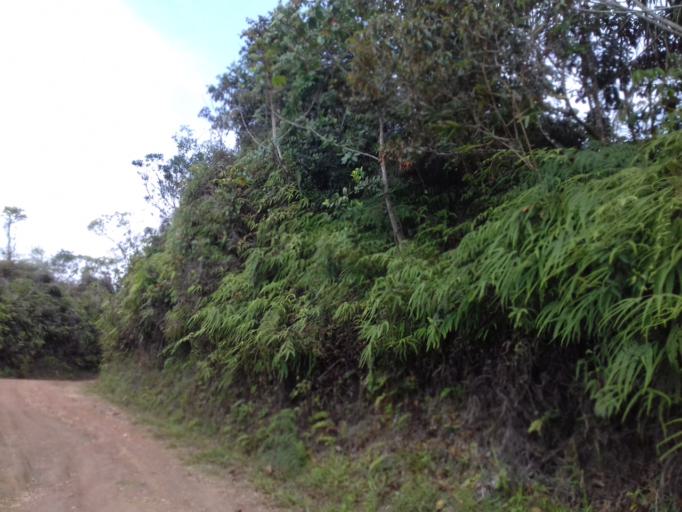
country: CO
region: Tolima
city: Libano
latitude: 4.9357
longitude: -75.0491
